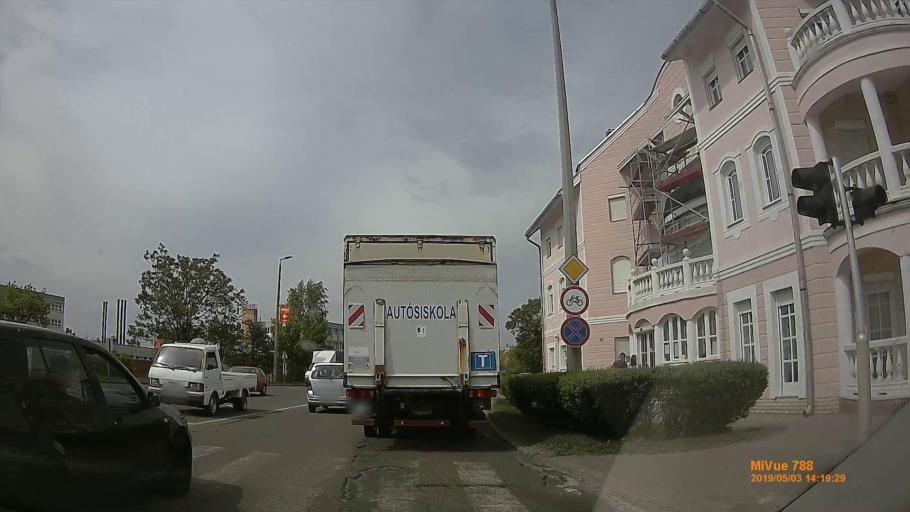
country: HU
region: Jasz-Nagykun-Szolnok
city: Szolnok
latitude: 47.1687
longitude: 20.1752
